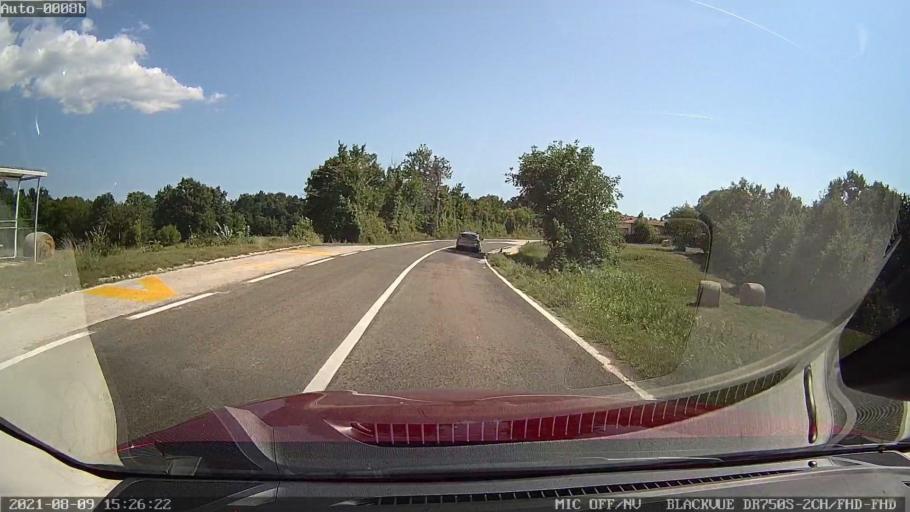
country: HR
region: Istarska
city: Pazin
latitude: 45.1626
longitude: 13.9074
